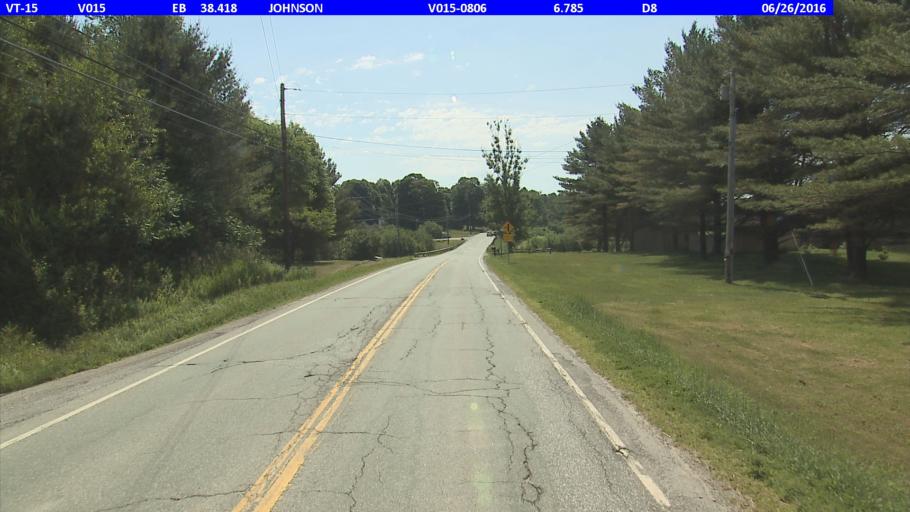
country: US
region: Vermont
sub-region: Lamoille County
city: Hyde Park
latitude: 44.6094
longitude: -72.6476
